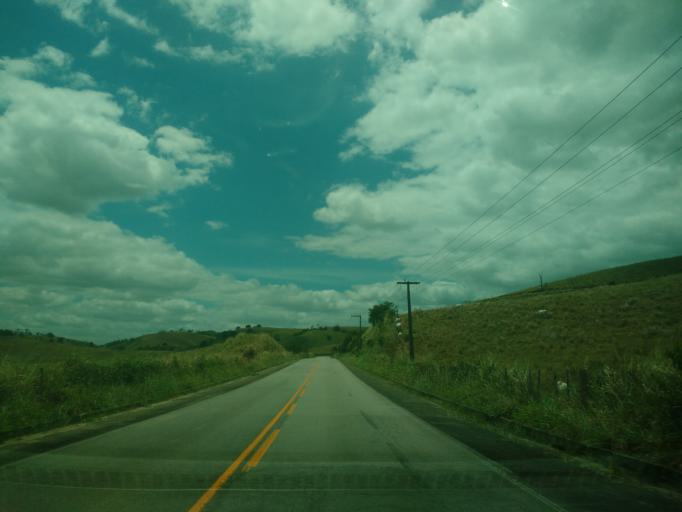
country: BR
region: Alagoas
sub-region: Uniao Dos Palmares
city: Uniao dos Palmares
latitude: -9.1375
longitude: -36.1143
